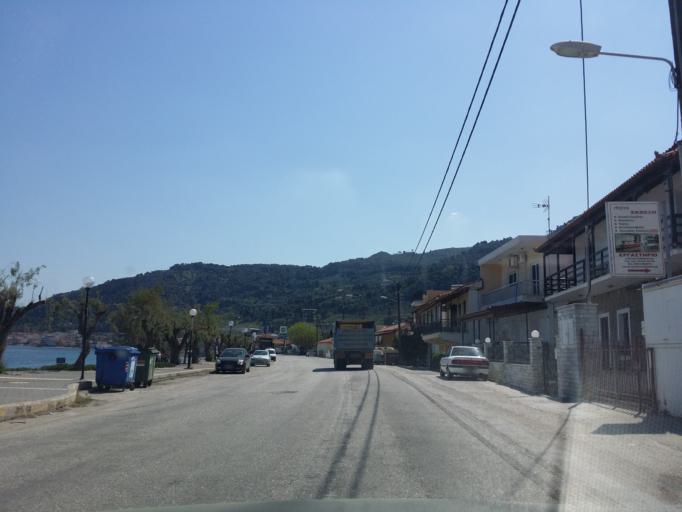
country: GR
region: West Greece
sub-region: Nomos Achaias
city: Aiyira
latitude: 38.1320
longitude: 22.4085
